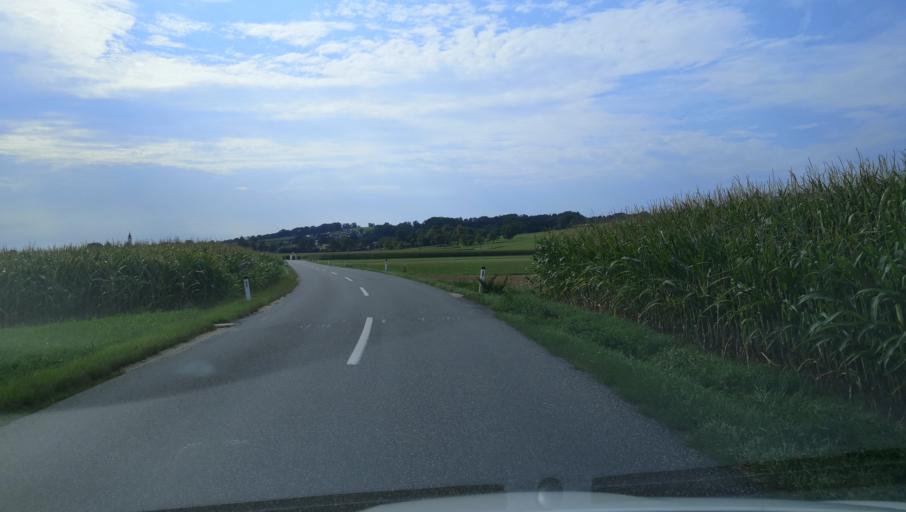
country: AT
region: Lower Austria
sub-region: Politischer Bezirk Melk
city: Blindenmarkt
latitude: 48.1302
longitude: 14.9719
